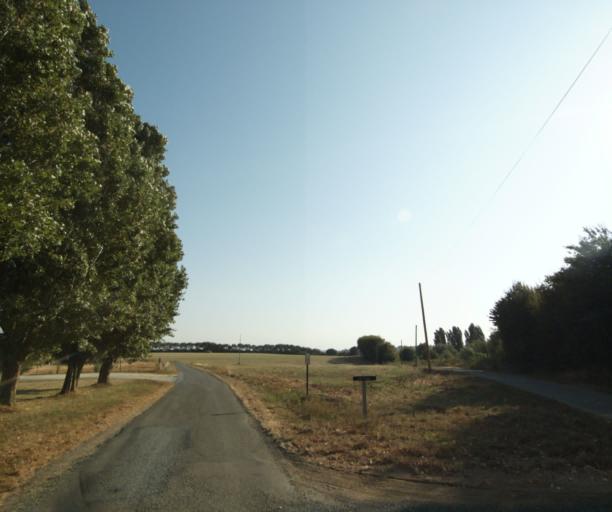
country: FR
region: Poitou-Charentes
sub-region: Departement de la Charente-Maritime
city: Cabariot
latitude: 45.9674
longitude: -0.8310
